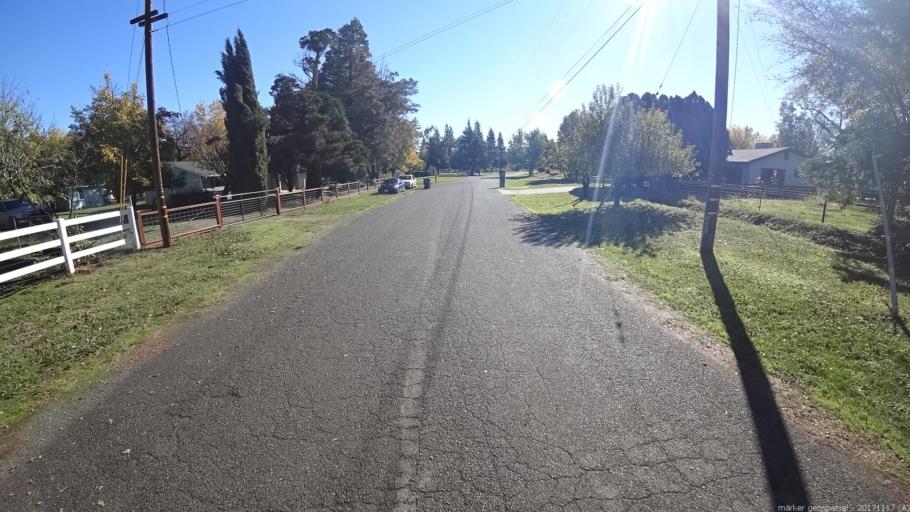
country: US
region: California
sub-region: Shasta County
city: Cottonwood
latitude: 40.4289
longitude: -122.2184
